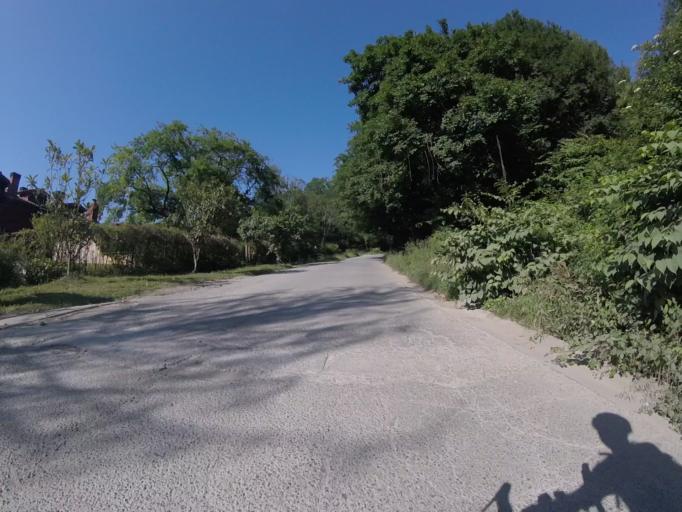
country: ES
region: Basque Country
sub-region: Provincia de Guipuzcoa
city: Astigarraga
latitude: 43.2921
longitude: -1.9398
